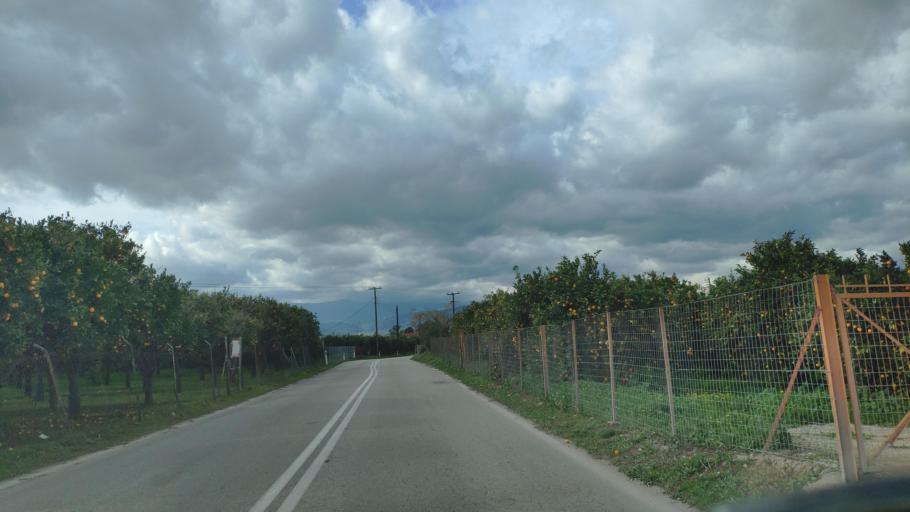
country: GR
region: Peloponnese
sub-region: Nomos Argolidos
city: Nea Tirins
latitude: 37.6085
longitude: 22.8056
